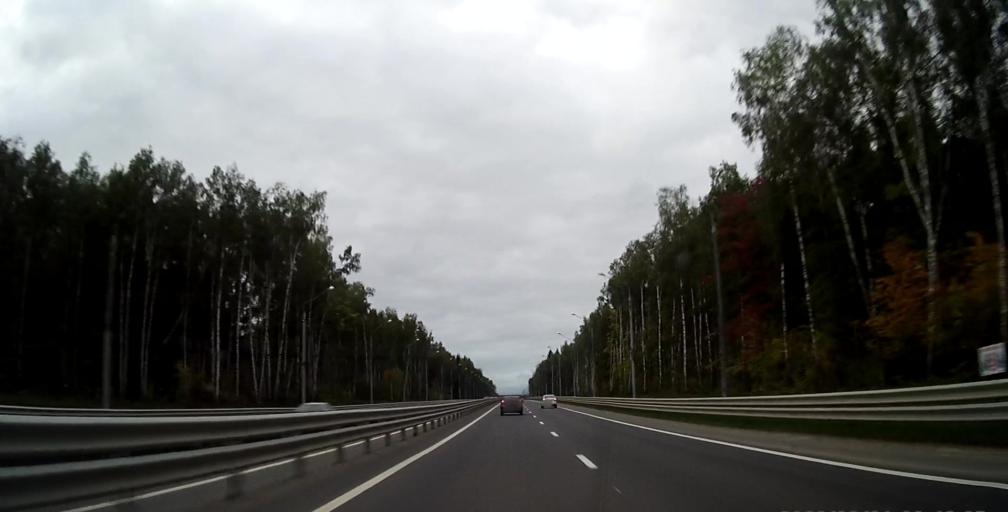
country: RU
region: Moskovskaya
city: Klimovsk
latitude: 55.3821
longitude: 37.5237
